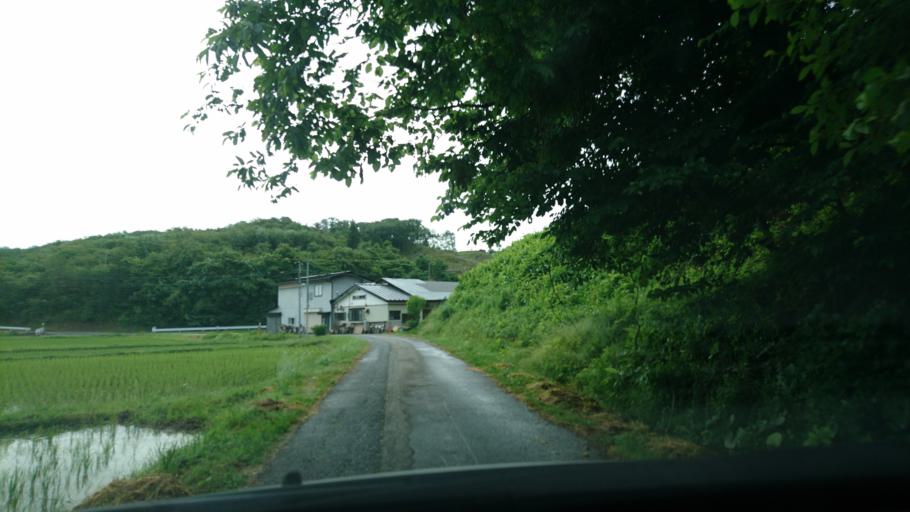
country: JP
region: Iwate
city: Ichinoseki
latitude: 38.8959
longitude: 141.1509
